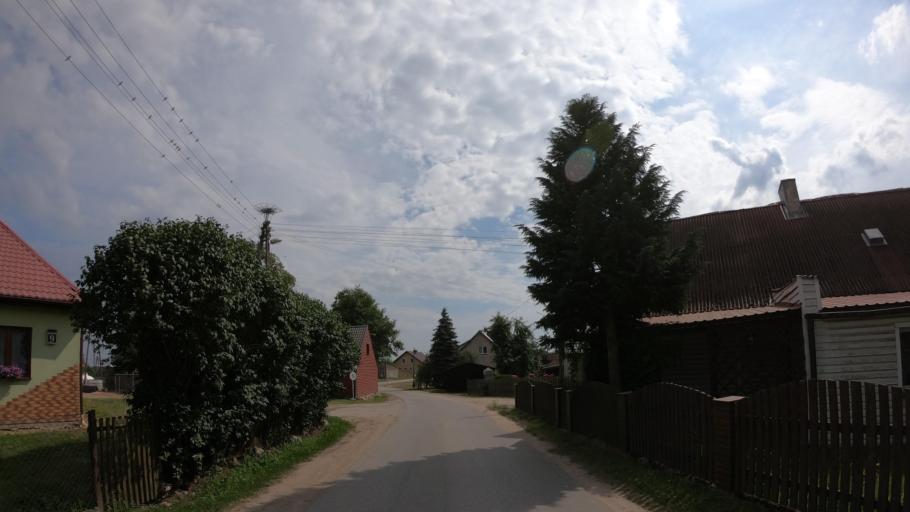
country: PL
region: West Pomeranian Voivodeship
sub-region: Powiat walecki
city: Tuczno
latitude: 53.2380
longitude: 16.1095
